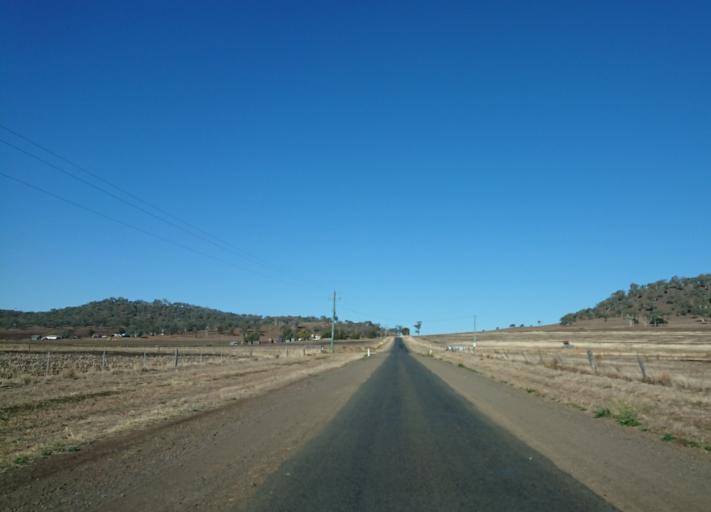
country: AU
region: Queensland
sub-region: Toowoomba
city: Top Camp
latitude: -27.8244
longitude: 152.0236
